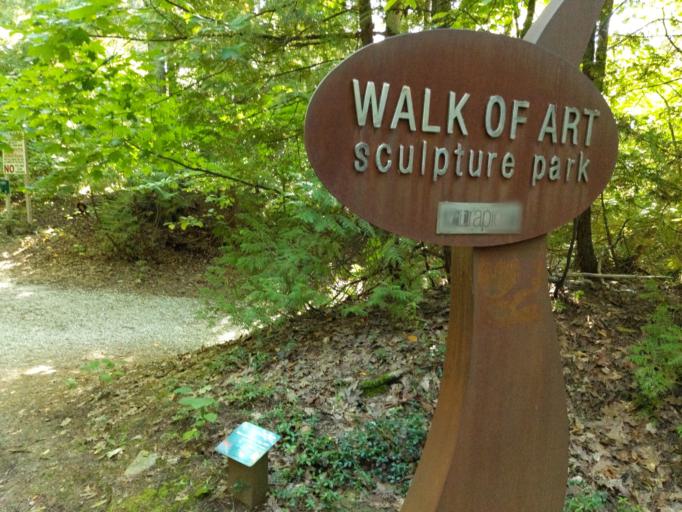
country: US
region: Michigan
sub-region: Antrim County
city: Elk Rapids
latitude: 44.8886
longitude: -85.4230
